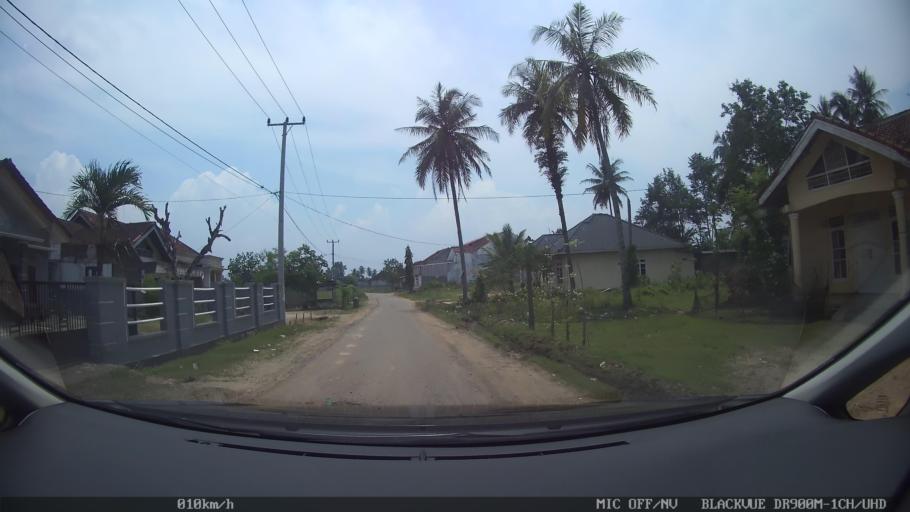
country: ID
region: Lampung
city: Natar
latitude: -5.3150
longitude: 105.2353
